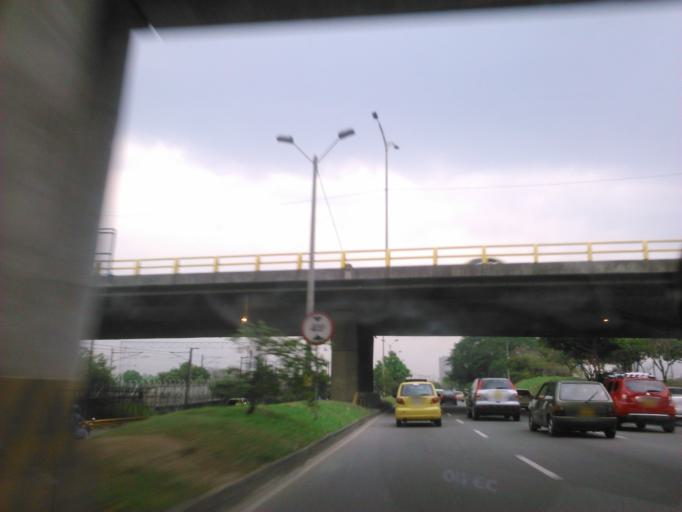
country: CO
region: Antioquia
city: Medellin
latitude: 6.2263
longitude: -75.5759
